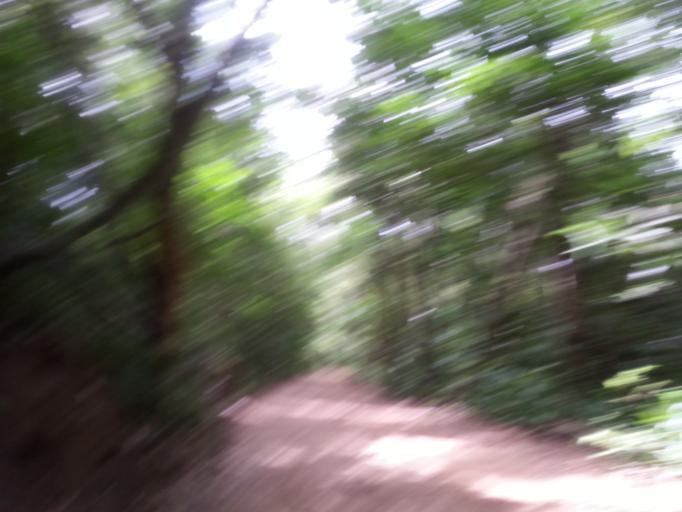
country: TH
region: Krabi
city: Khlong Thom
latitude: 7.9252
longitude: 99.2614
